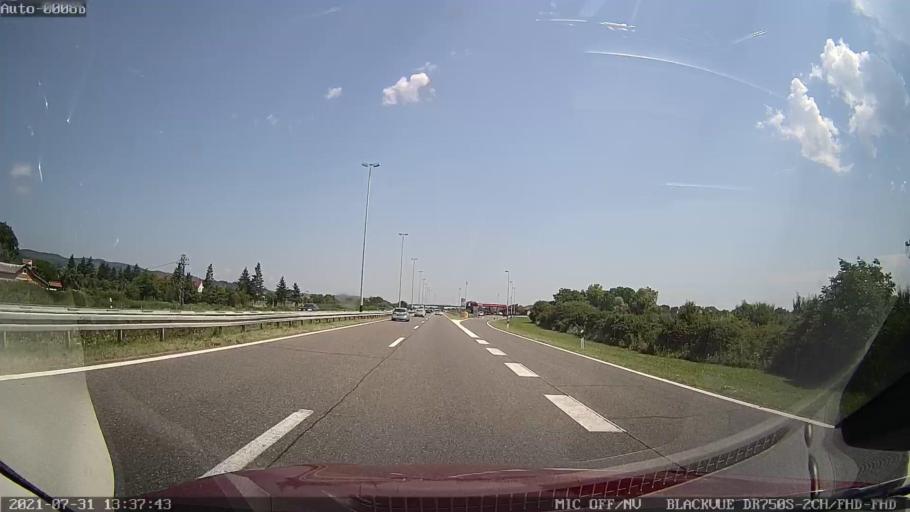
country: HR
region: Brodsko-Posavska
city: Luzani
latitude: 45.1638
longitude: 17.6983
